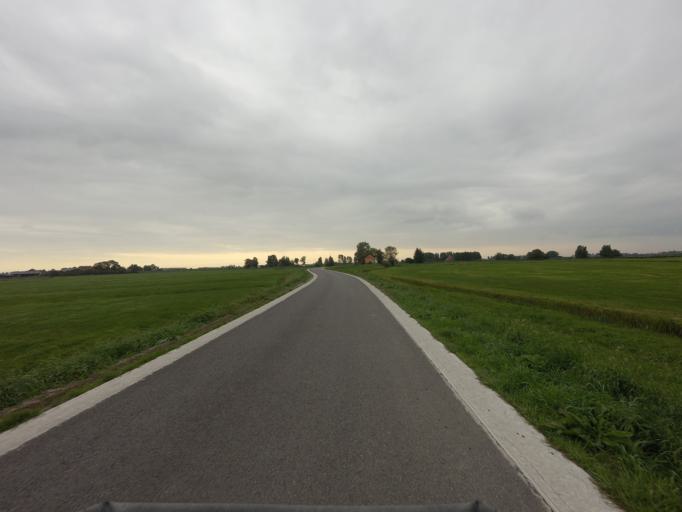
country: NL
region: Friesland
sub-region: Sudwest Fryslan
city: IJlst
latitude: 53.0088
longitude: 5.5860
